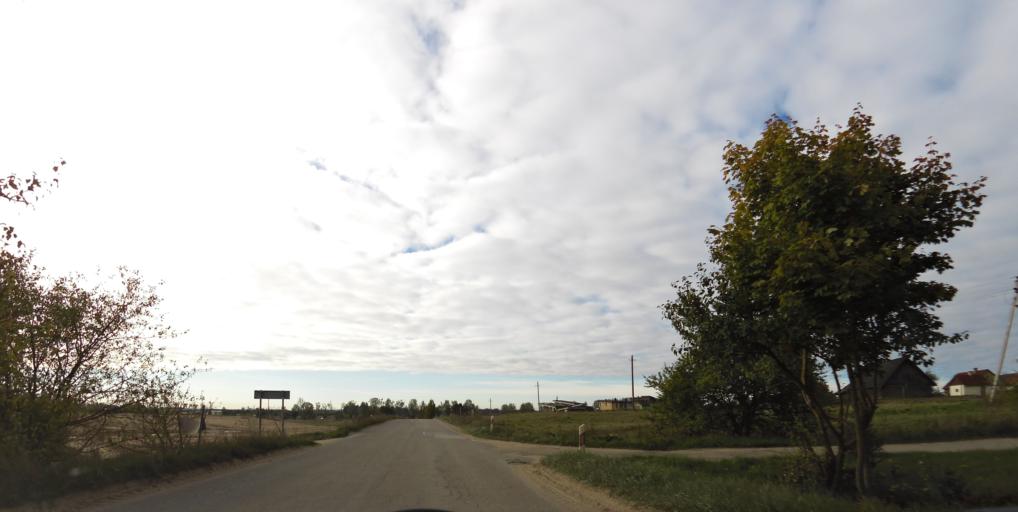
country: LT
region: Vilnius County
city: Pilaite
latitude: 54.7281
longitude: 25.1534
